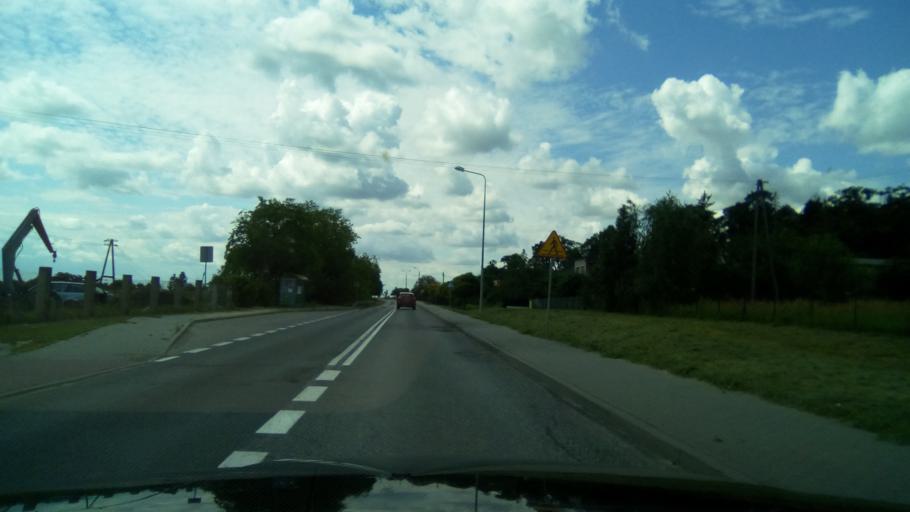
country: PL
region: Kujawsko-Pomorskie
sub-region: Powiat nakielski
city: Szubin
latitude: 53.0178
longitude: 17.7581
